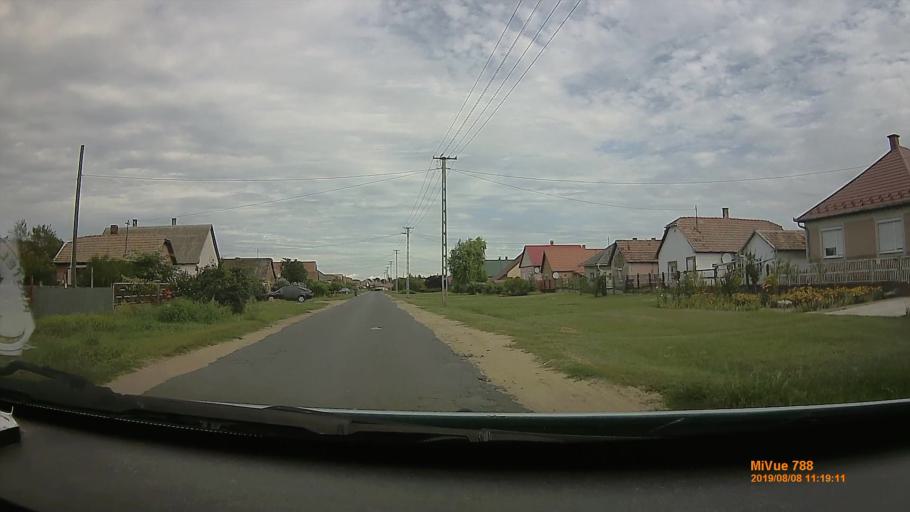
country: HU
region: Szabolcs-Szatmar-Bereg
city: Balkany
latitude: 47.7435
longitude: 21.8392
